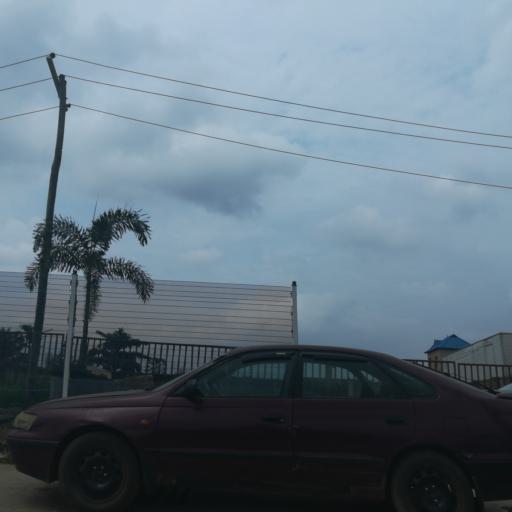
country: NG
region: Lagos
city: Ojota
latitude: 6.5850
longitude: 3.3896
